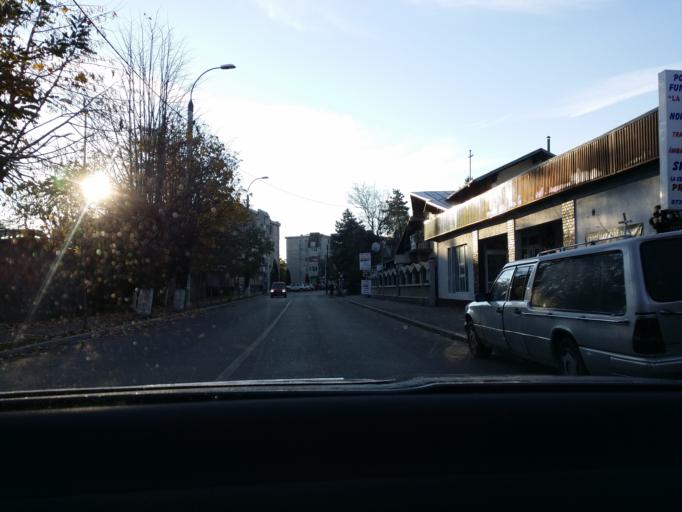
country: RO
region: Prahova
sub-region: Municipiul Campina
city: Campina
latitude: 45.1321
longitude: 25.7330
